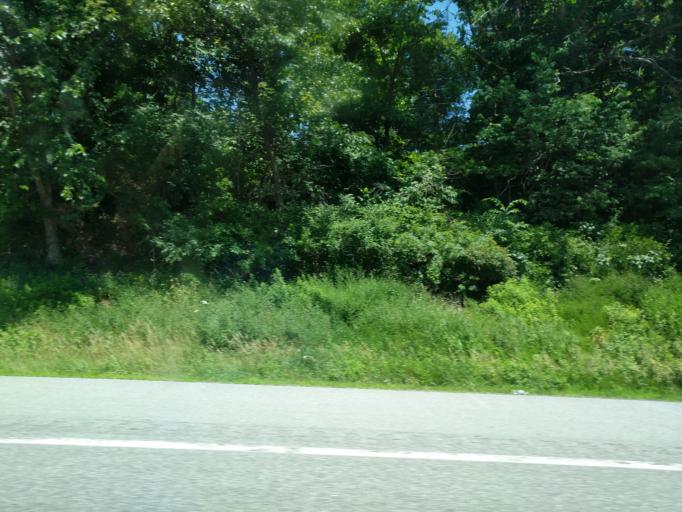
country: US
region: New York
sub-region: Orange County
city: Harriman
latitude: 41.3222
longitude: -74.1515
